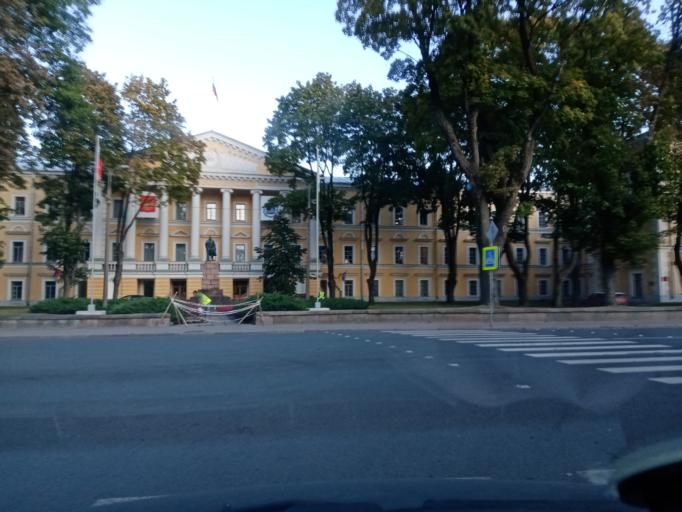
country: RU
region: Pskov
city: Pskov
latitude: 57.8161
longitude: 28.3411
